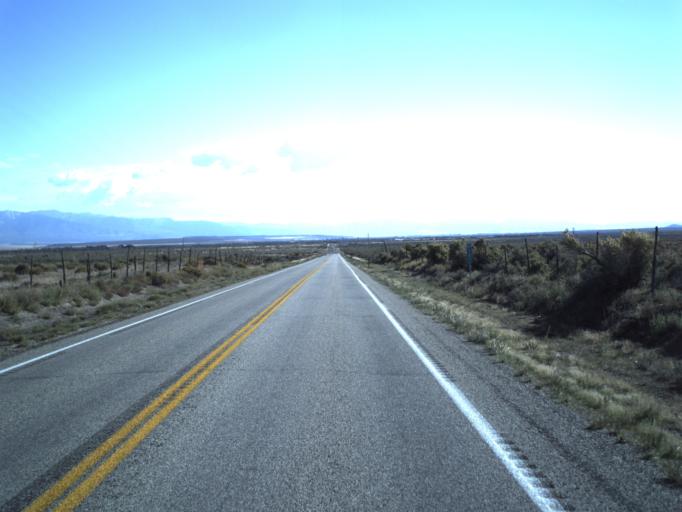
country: US
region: Utah
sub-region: Millard County
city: Fillmore
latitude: 39.1652
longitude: -112.4101
